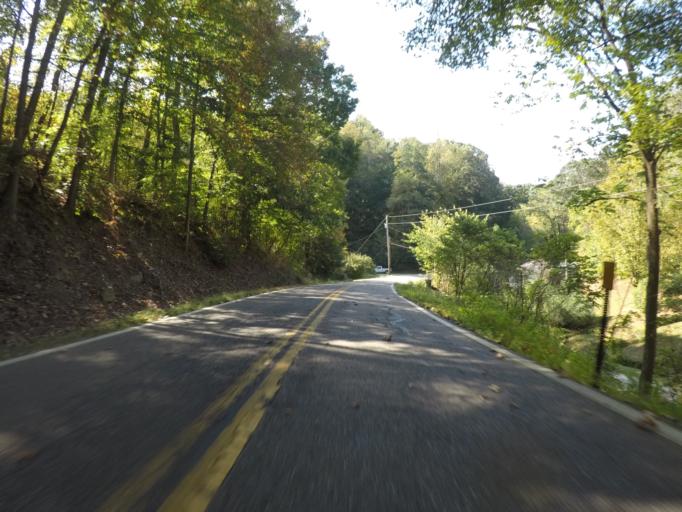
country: US
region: West Virginia
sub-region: Cabell County
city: Lesage
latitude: 38.6463
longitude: -82.4238
